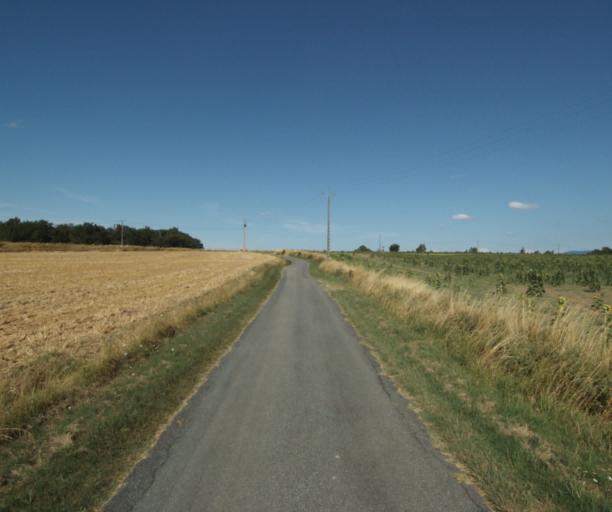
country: FR
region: Midi-Pyrenees
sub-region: Departement de la Haute-Garonne
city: Revel
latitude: 43.5005
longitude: 1.9744
